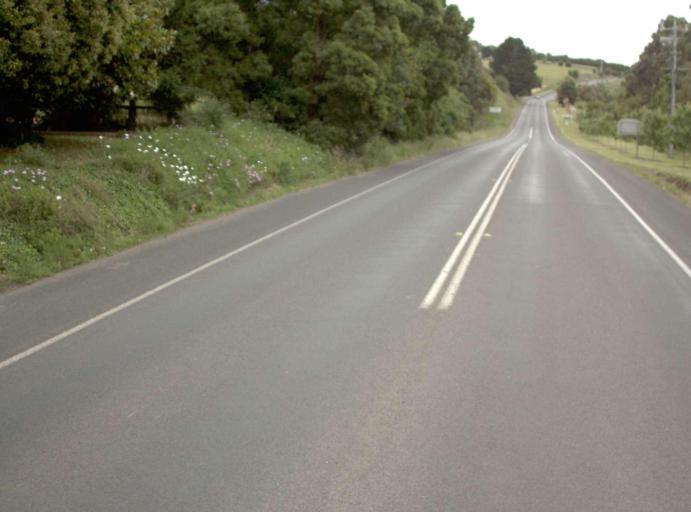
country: AU
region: Victoria
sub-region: Baw Baw
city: Warragul
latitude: -38.4704
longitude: 145.9406
